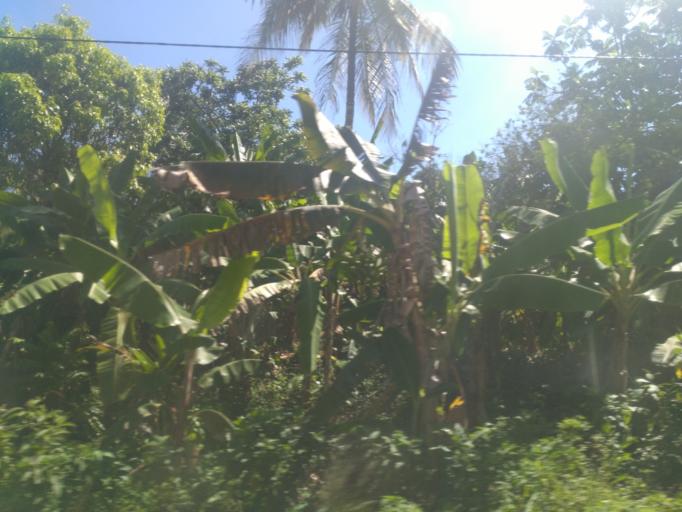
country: TZ
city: Kiwengwa
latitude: -5.9835
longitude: 39.3305
